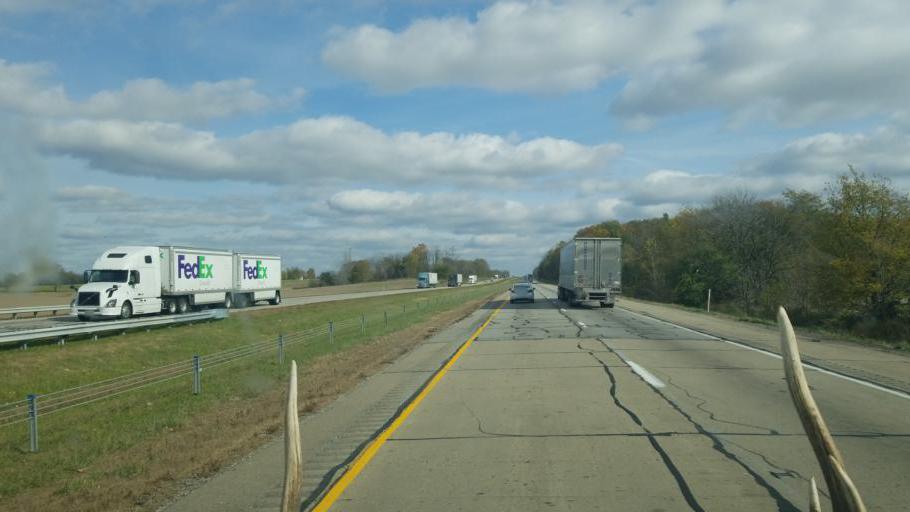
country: US
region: Indiana
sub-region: Henry County
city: New Castle
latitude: 39.8528
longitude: -85.3492
